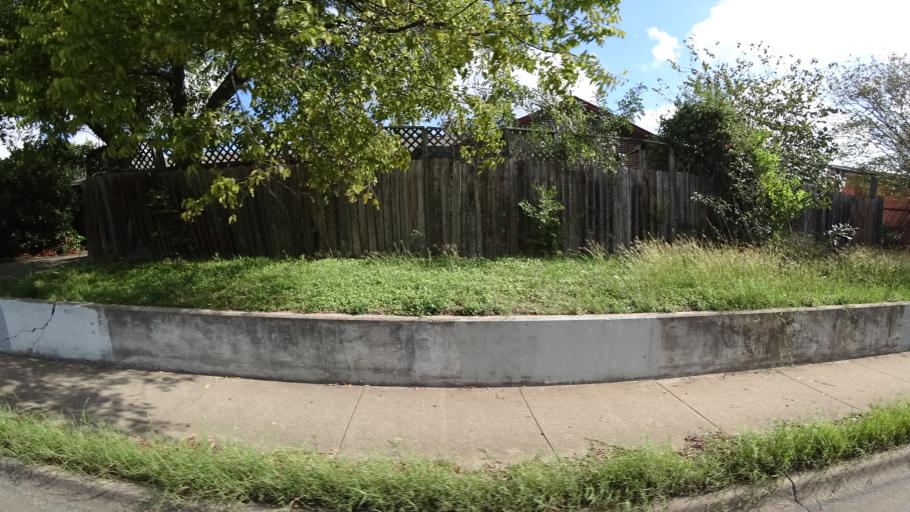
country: US
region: Texas
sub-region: Travis County
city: Shady Hollow
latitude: 30.2036
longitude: -97.8087
